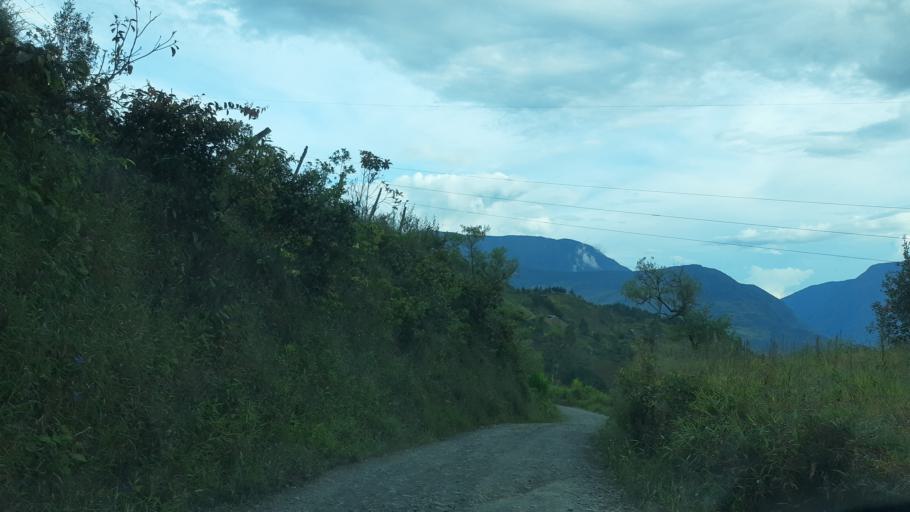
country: CO
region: Boyaca
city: Garagoa
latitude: 4.9863
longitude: -73.3256
